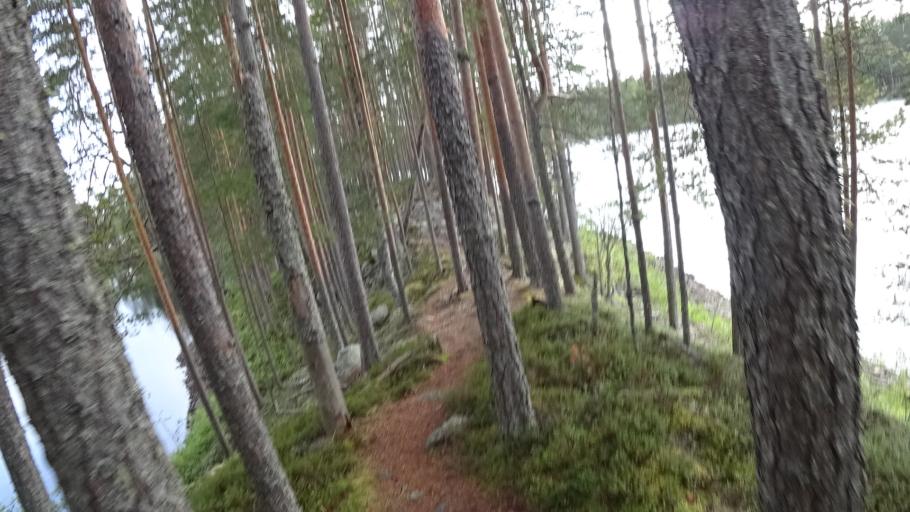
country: FI
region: North Karelia
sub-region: Joensuu
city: Ilomantsi
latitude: 62.5748
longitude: 31.1727
